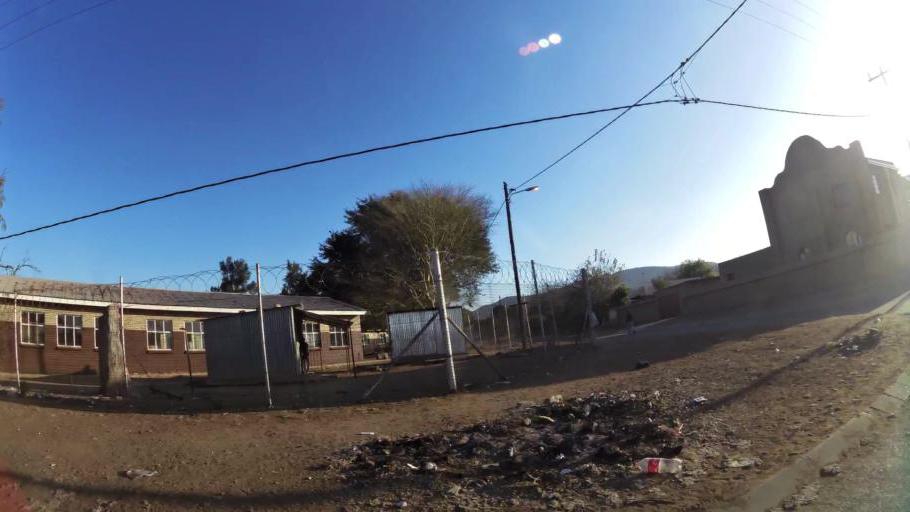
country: ZA
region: North-West
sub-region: Bojanala Platinum District Municipality
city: Rustenburg
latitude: -25.6419
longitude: 27.2198
